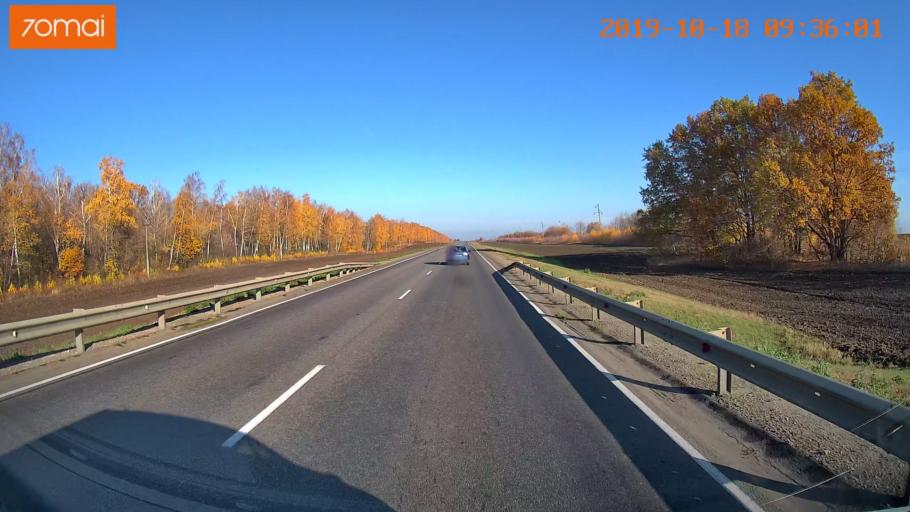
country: RU
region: Tula
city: Yefremov
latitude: 53.2001
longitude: 38.1466
